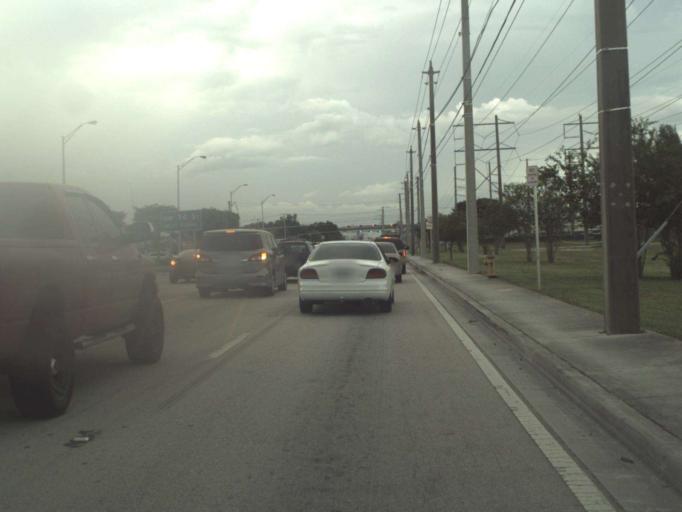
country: US
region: Florida
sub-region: Miami-Dade County
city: Miami Springs
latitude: 25.8378
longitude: -80.3139
